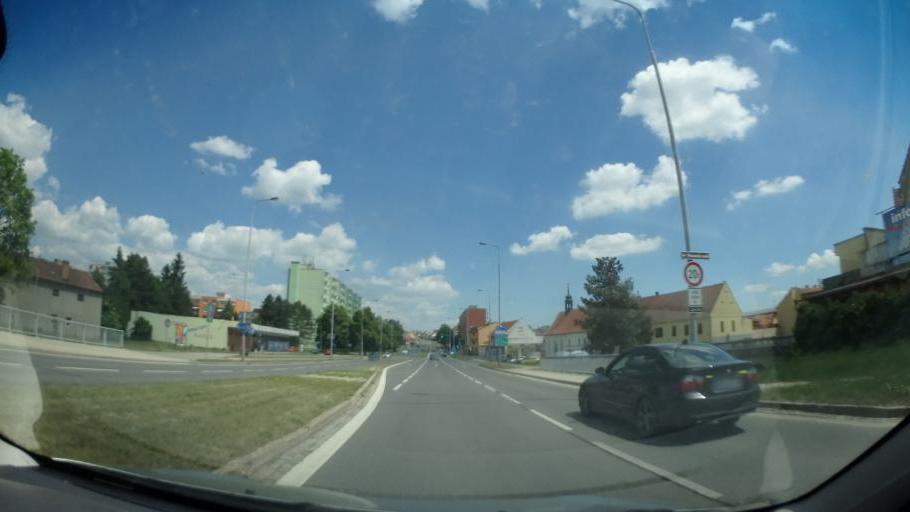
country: CZ
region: South Moravian
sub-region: Okres Vyskov
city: Vyskov
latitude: 49.2798
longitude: 16.9988
